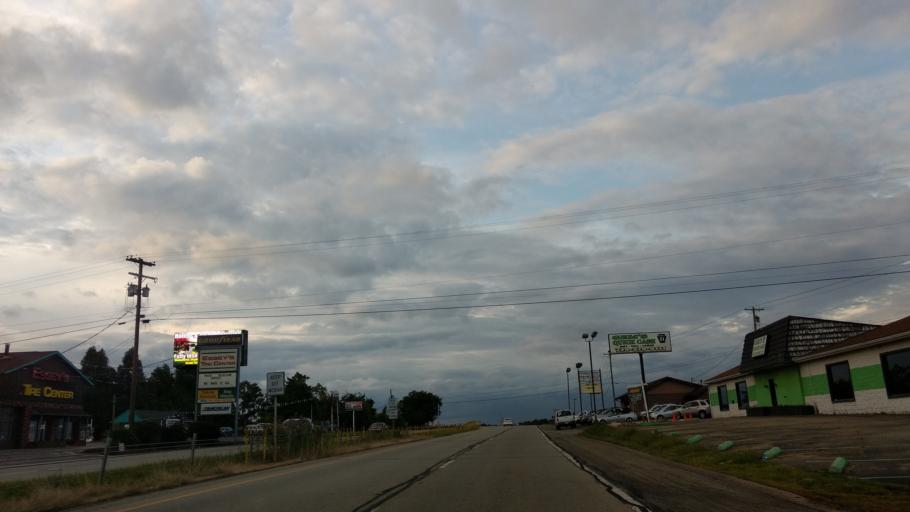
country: US
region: Pennsylvania
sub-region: Westmoreland County
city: Fellsburg
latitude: 40.2095
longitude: -79.8407
